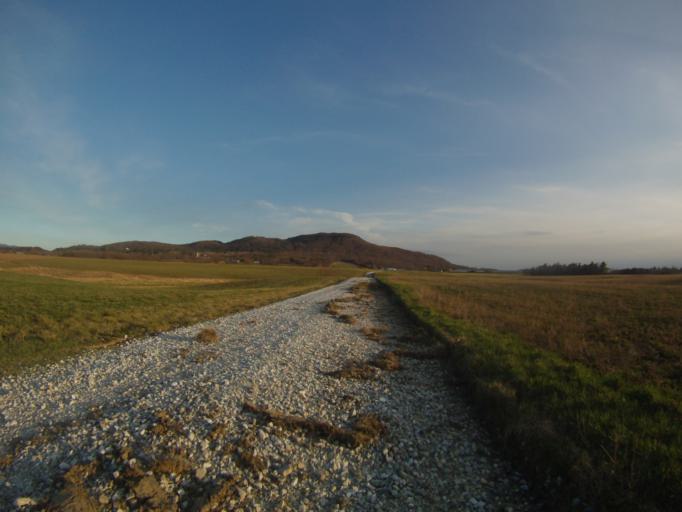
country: US
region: Vermont
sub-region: Addison County
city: Vergennes
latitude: 44.0975
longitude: -73.2843
